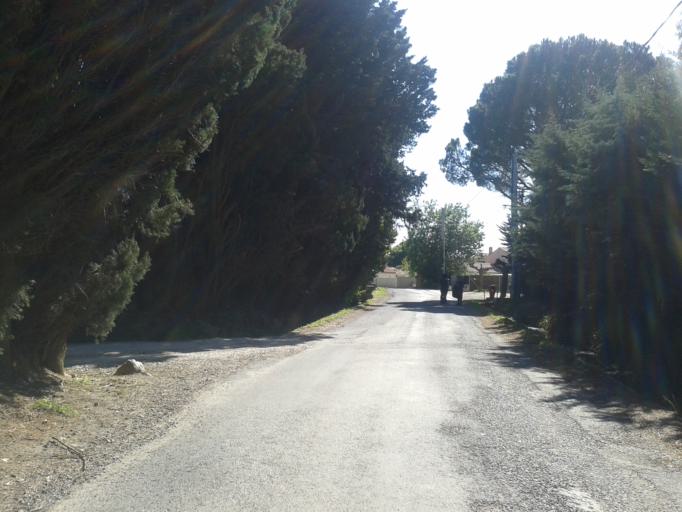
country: FR
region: Languedoc-Roussillon
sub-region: Departement des Pyrenees-Orientales
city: Pezilla-la-Riviere
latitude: 42.6992
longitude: 2.7710
